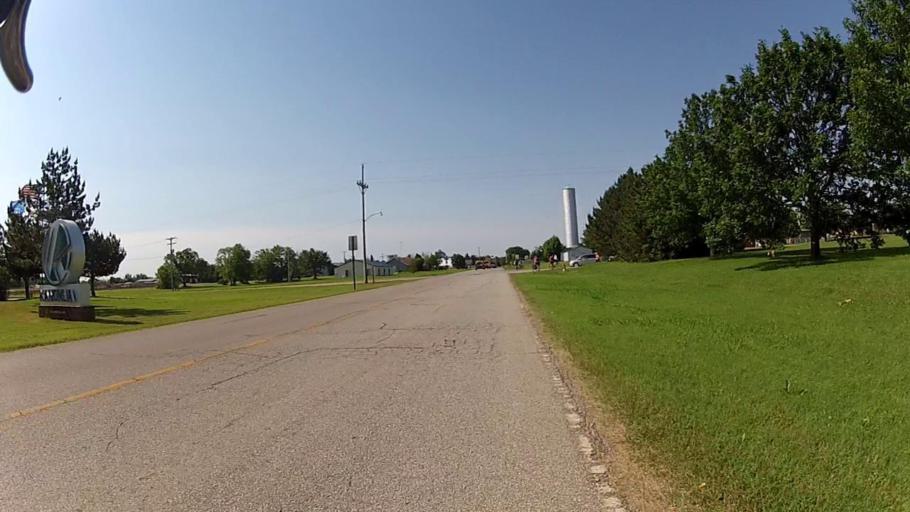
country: US
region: Kansas
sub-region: Sumner County
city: Caldwell
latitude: 37.0422
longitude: -97.6070
